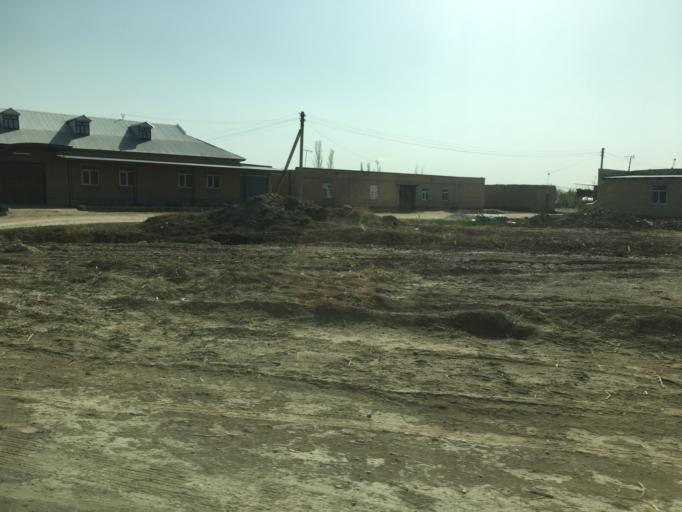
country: TM
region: Lebap
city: Farap
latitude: 39.2955
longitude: 63.4101
